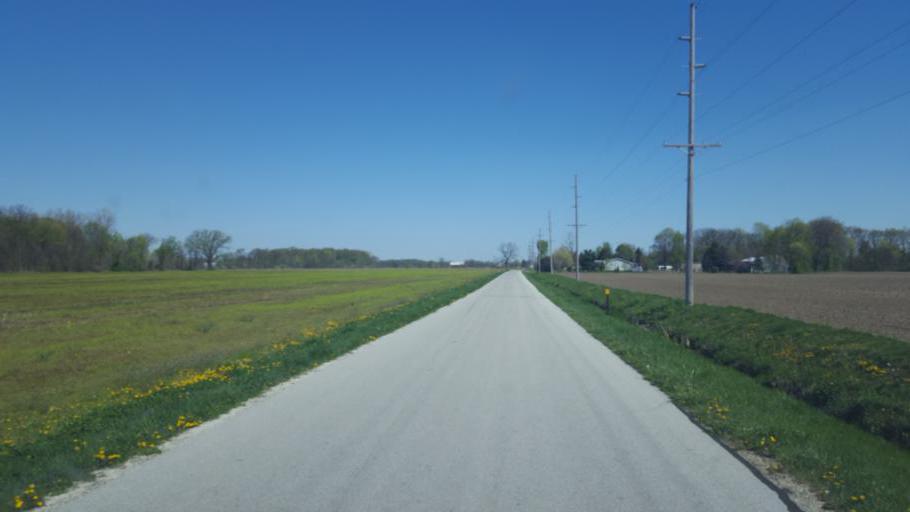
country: US
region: Ohio
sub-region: Sandusky County
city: Ballville
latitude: 41.2513
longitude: -83.1875
